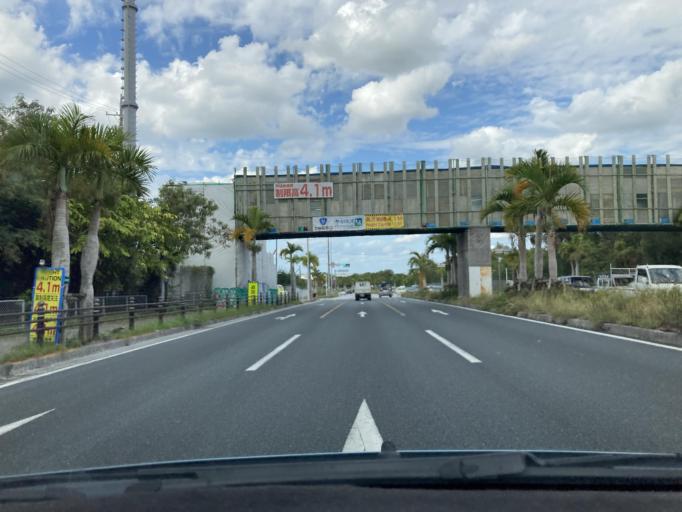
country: JP
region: Okinawa
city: Chatan
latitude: 26.3358
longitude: 127.7514
